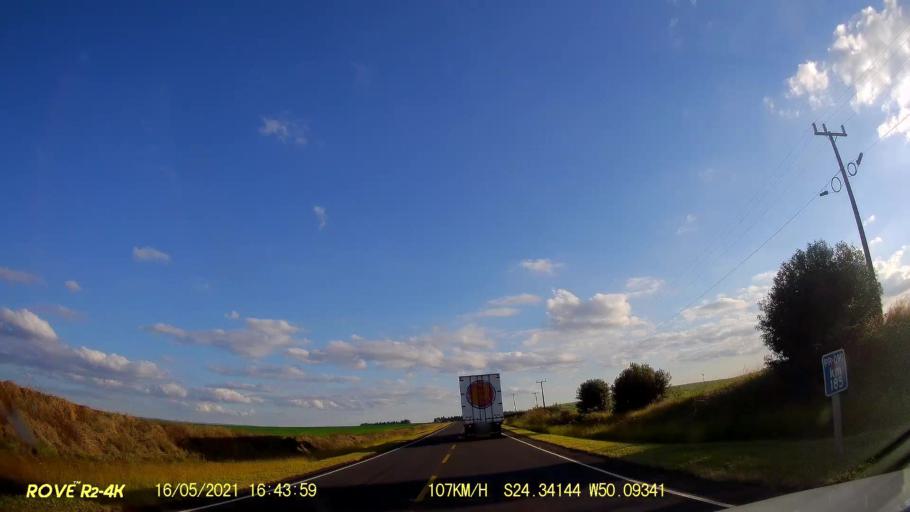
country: BR
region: Parana
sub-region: Pirai Do Sul
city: Pirai do Sul
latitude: -24.3416
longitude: -50.0936
